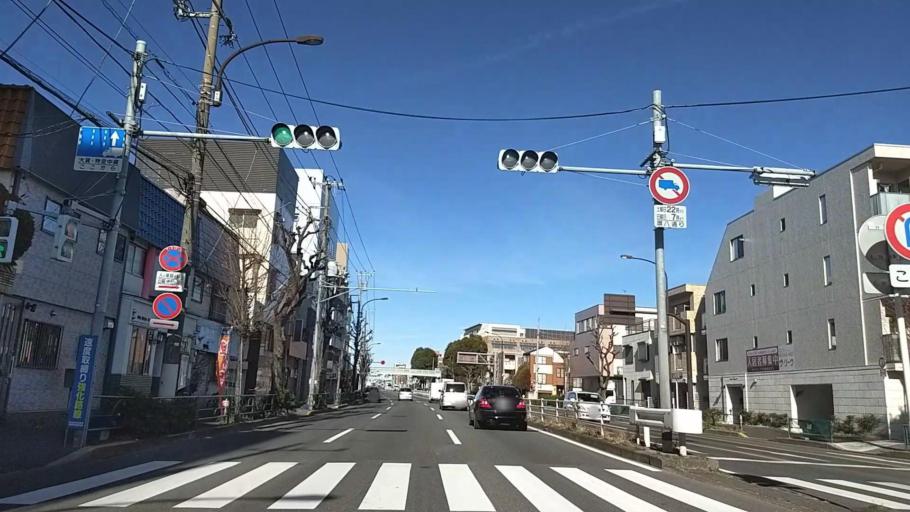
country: JP
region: Kanagawa
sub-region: Kawasaki-shi
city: Kawasaki
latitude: 35.5936
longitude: 139.6746
